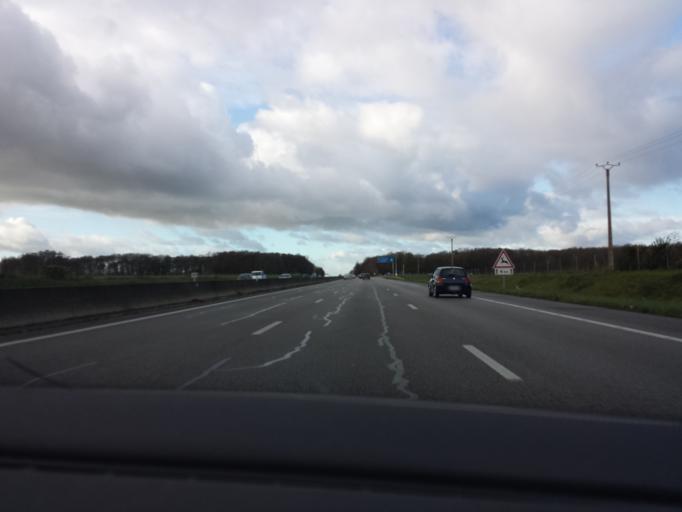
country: FR
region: Ile-de-France
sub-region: Departement des Yvelines
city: Bennecourt
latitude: 49.0212
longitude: 1.5534
